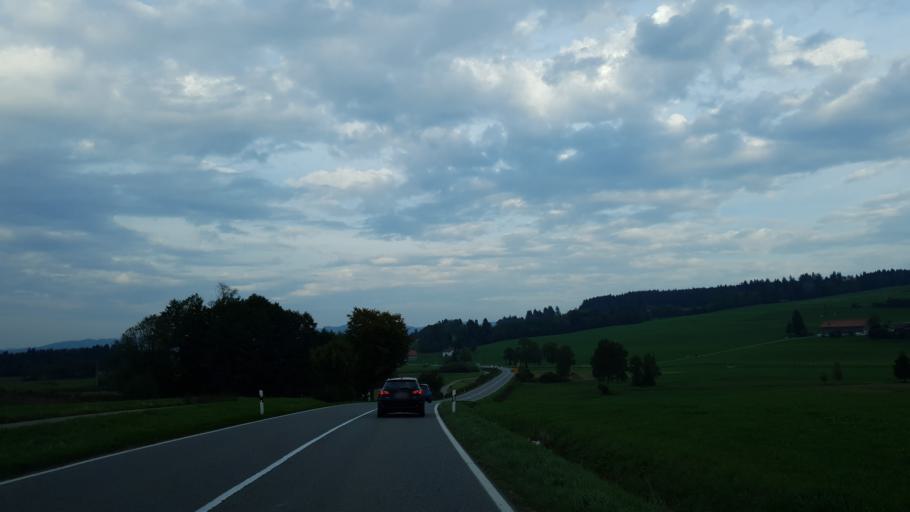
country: DE
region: Bavaria
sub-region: Swabia
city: Gestratz
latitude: 47.6792
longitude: 9.9892
